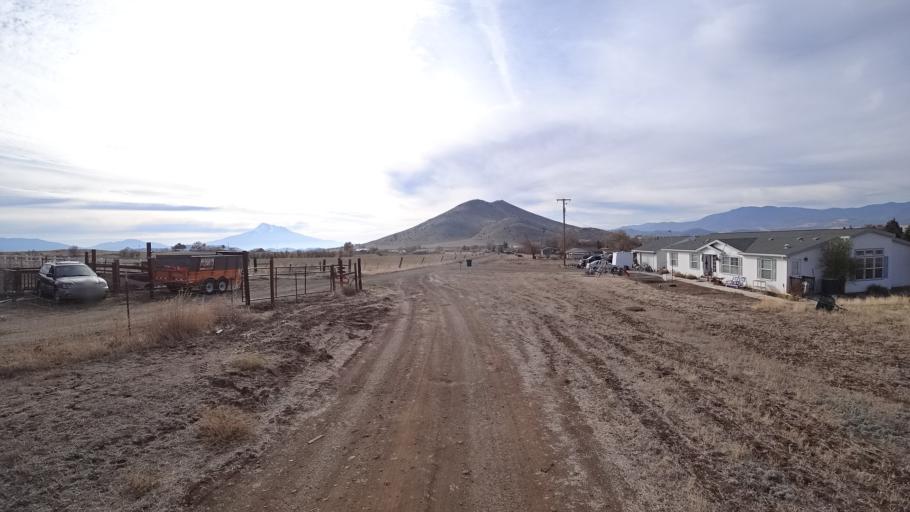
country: US
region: California
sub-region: Siskiyou County
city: Montague
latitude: 41.7295
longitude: -122.5155
